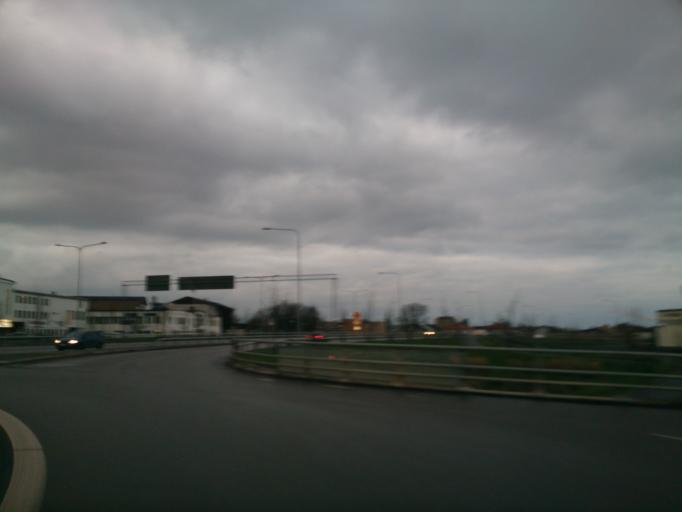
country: SE
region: OEstergoetland
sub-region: Linkopings Kommun
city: Linkoping
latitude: 58.4015
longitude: 15.6531
